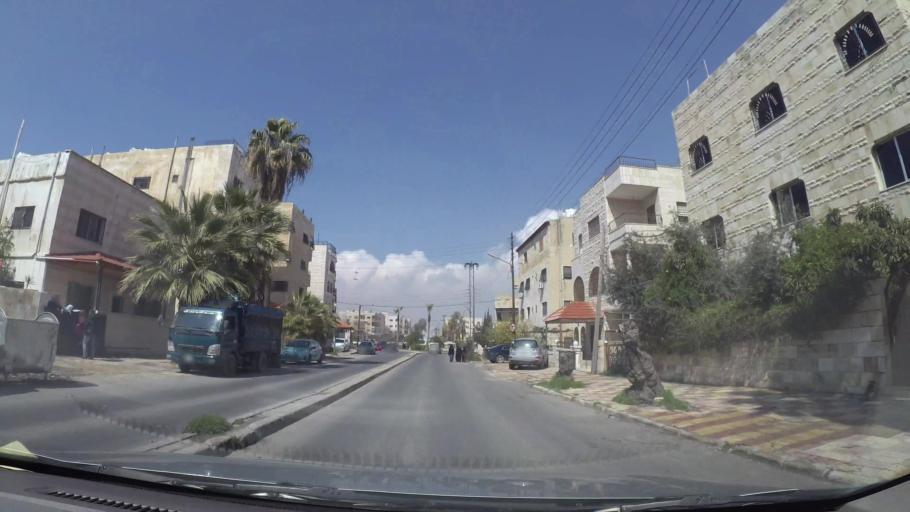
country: JO
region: Amman
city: Al Bunayyat ash Shamaliyah
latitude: 31.9288
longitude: 35.9048
